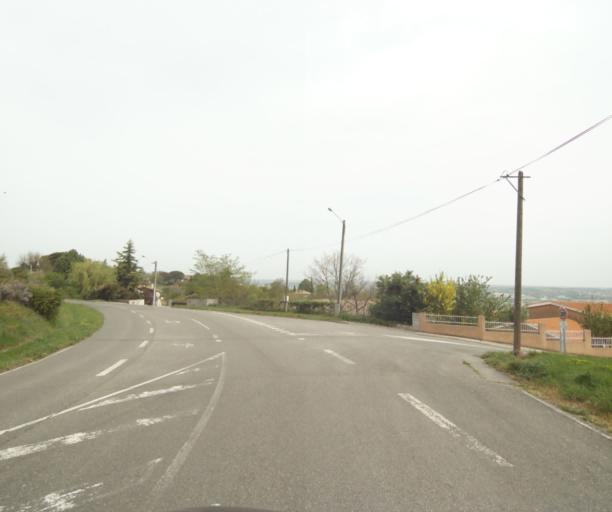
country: FR
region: Midi-Pyrenees
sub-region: Departement de la Haute-Garonne
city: Pechabou
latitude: 43.5025
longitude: 1.5029
